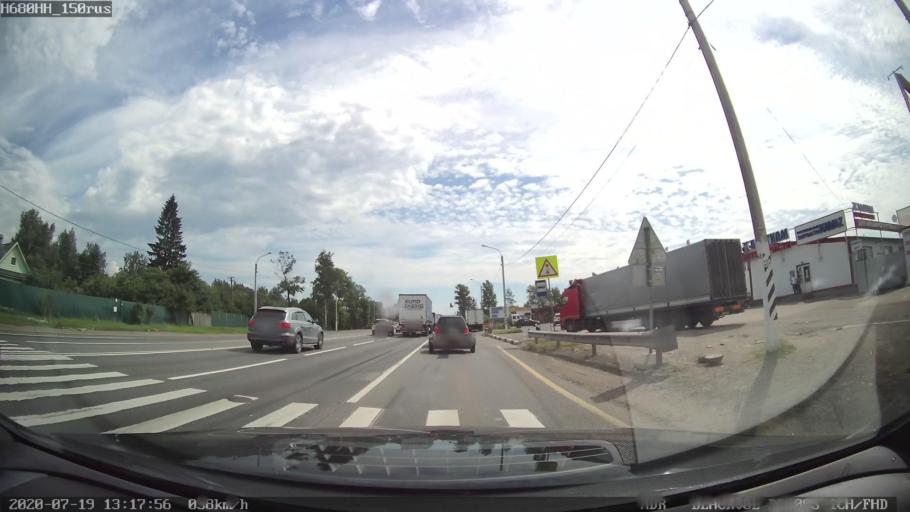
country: RU
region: St.-Petersburg
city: Kolpino
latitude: 59.7052
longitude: 30.5766
